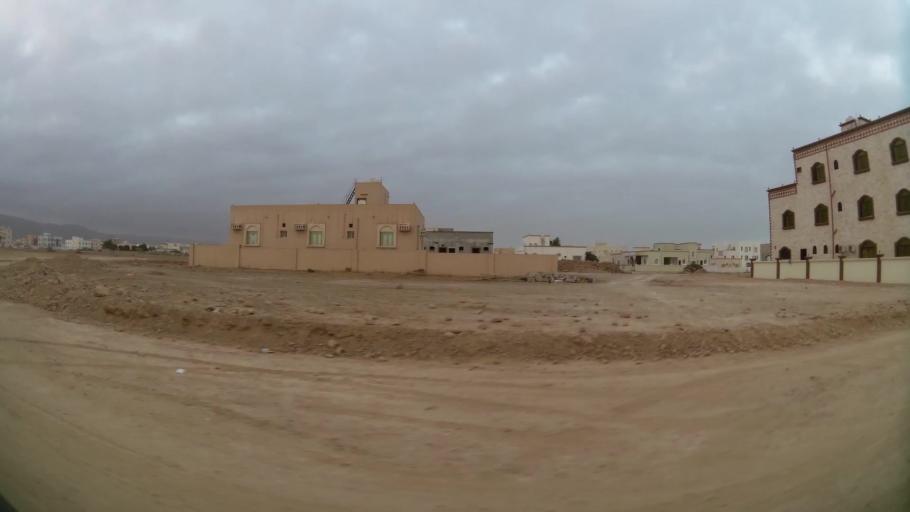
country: OM
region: Zufar
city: Salalah
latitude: 17.0369
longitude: 54.0314
